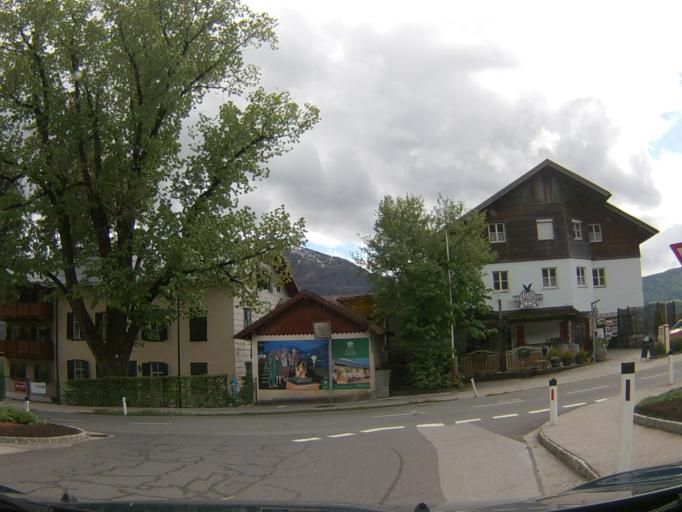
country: AT
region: Upper Austria
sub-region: Politischer Bezirk Gmunden
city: Sankt Wolfgang im Salzkammergut
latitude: 47.7368
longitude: 13.4530
